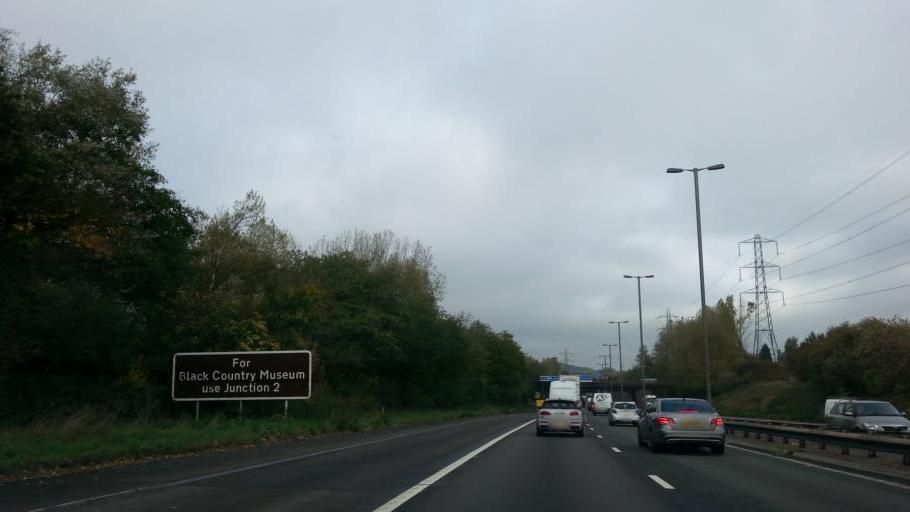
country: GB
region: England
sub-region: Sandwell
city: Rowley Regis
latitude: 52.4775
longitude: -2.0217
